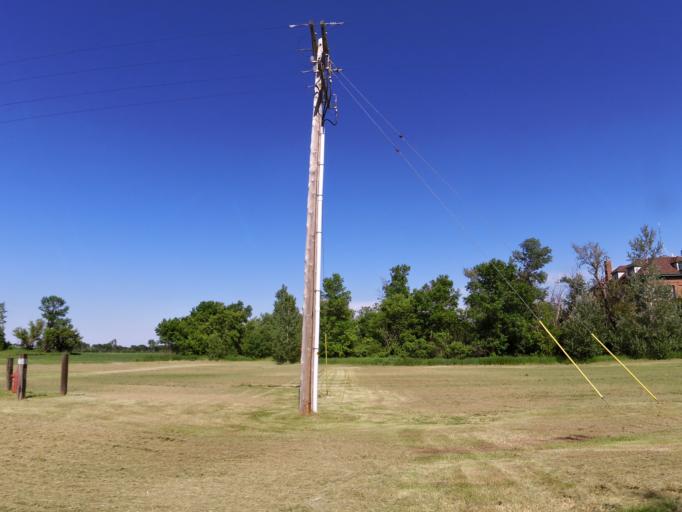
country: US
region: North Dakota
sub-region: Walsh County
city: Grafton
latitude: 48.2961
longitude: -97.2547
